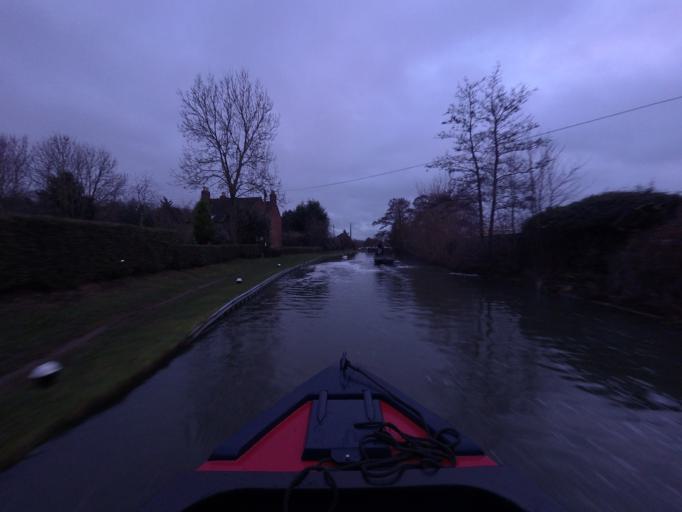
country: GB
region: England
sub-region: Northamptonshire
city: Long Buckby
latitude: 52.2746
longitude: -1.0955
